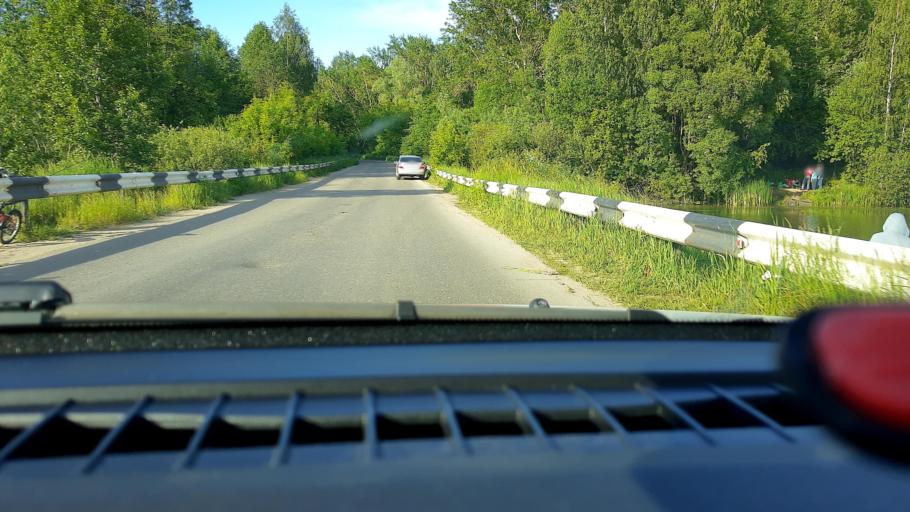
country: RU
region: Nizjnij Novgorod
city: Gorbatovka
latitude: 56.2231
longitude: 43.7551
